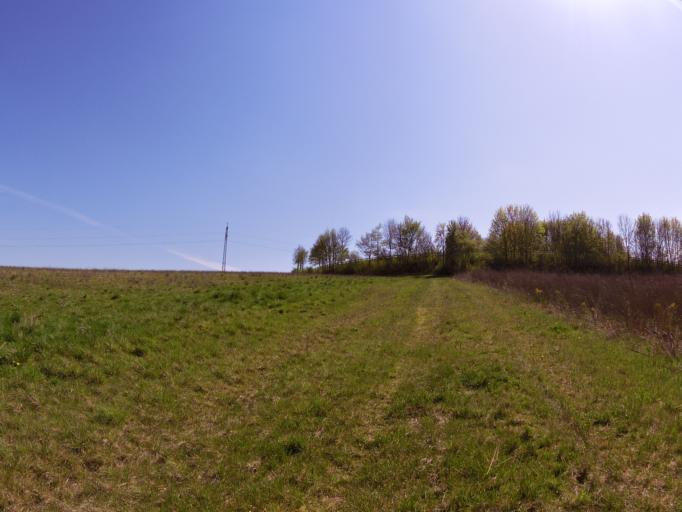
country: DE
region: Bavaria
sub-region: Regierungsbezirk Unterfranken
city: Kurnach
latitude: 49.8581
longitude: 10.0199
